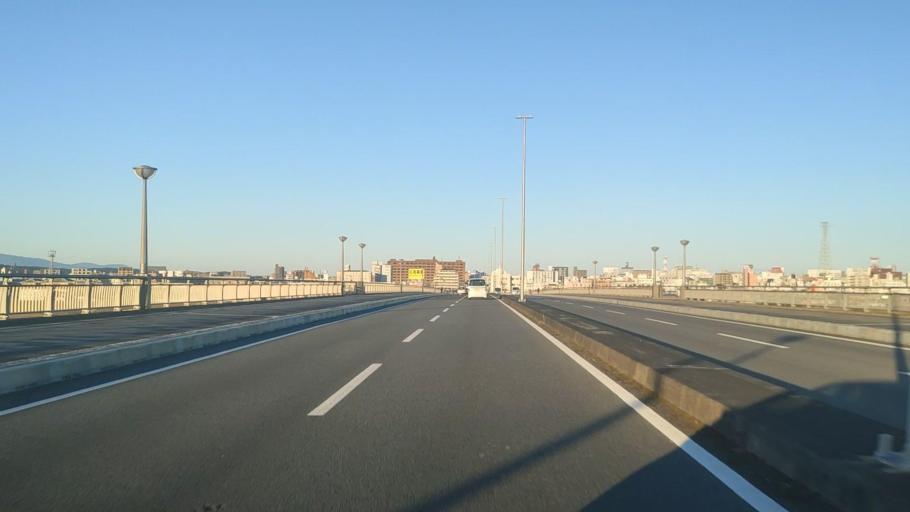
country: JP
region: Miyazaki
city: Miyazaki-shi
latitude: 31.9072
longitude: 131.4105
